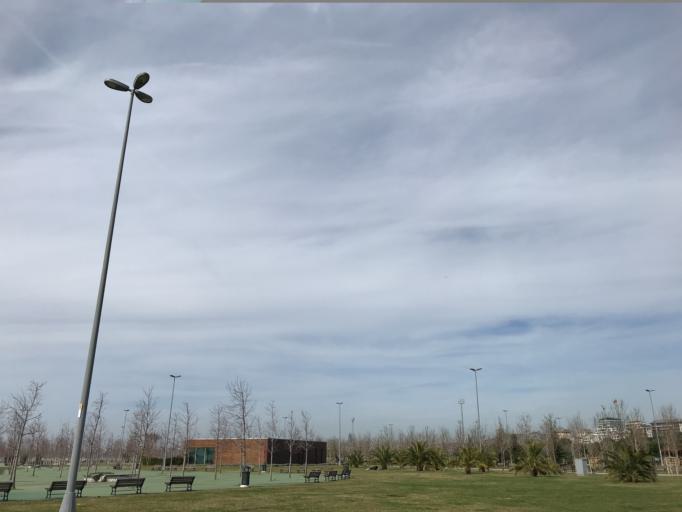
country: TR
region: Istanbul
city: Maltepe
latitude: 40.9257
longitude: 29.1175
